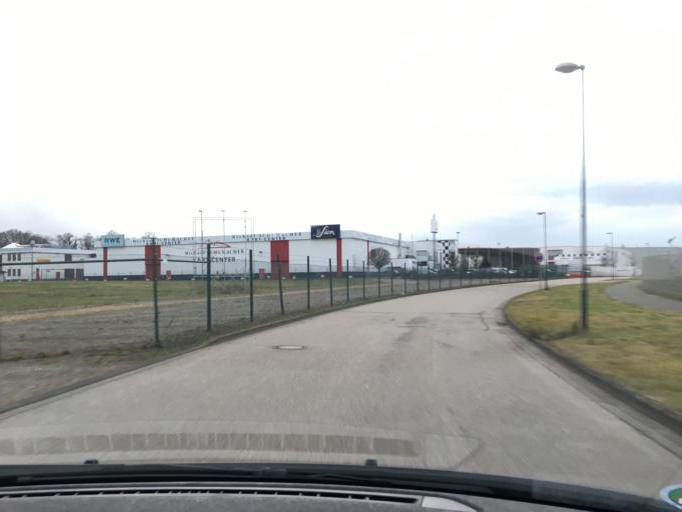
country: DE
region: North Rhine-Westphalia
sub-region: Regierungsbezirk Koln
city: Kerpen
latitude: 50.8918
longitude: 6.6765
